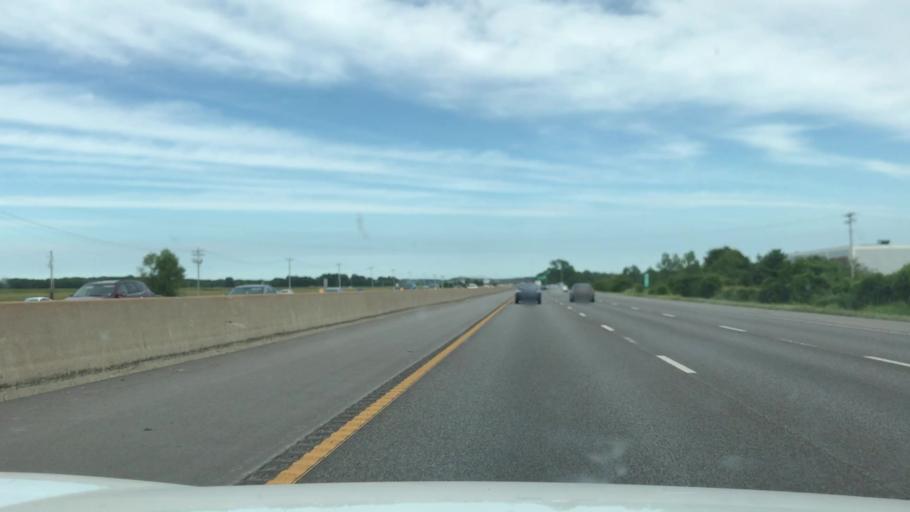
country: US
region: Missouri
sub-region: Saint Louis County
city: Chesterfield
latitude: 38.6729
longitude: -90.6291
